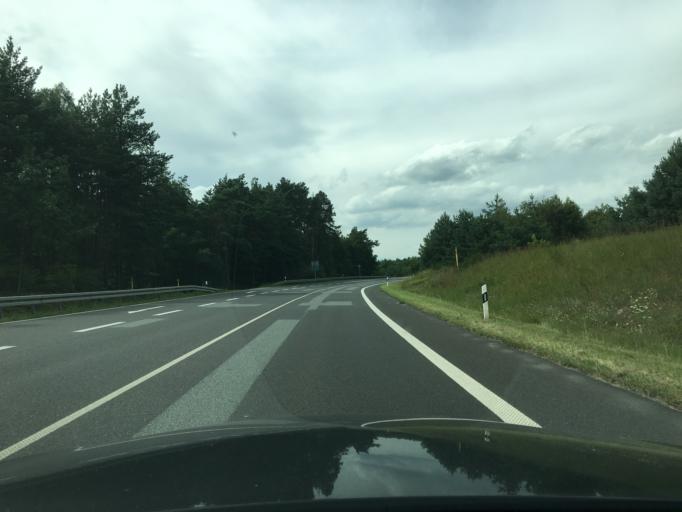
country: DE
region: Mecklenburg-Vorpommern
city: Neustrelitz
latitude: 53.3727
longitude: 13.0823
